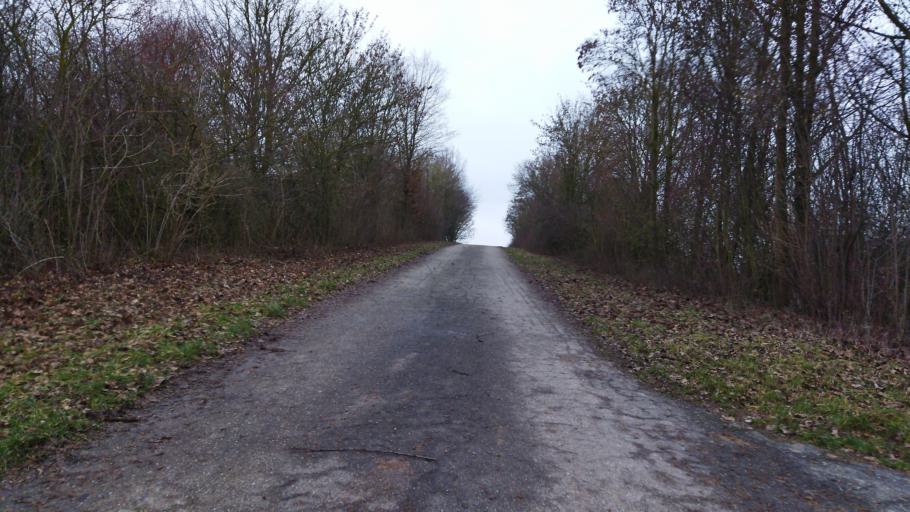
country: DE
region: Baden-Wuerttemberg
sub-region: Regierungsbezirk Stuttgart
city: Nordheim
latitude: 49.1174
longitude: 9.1462
